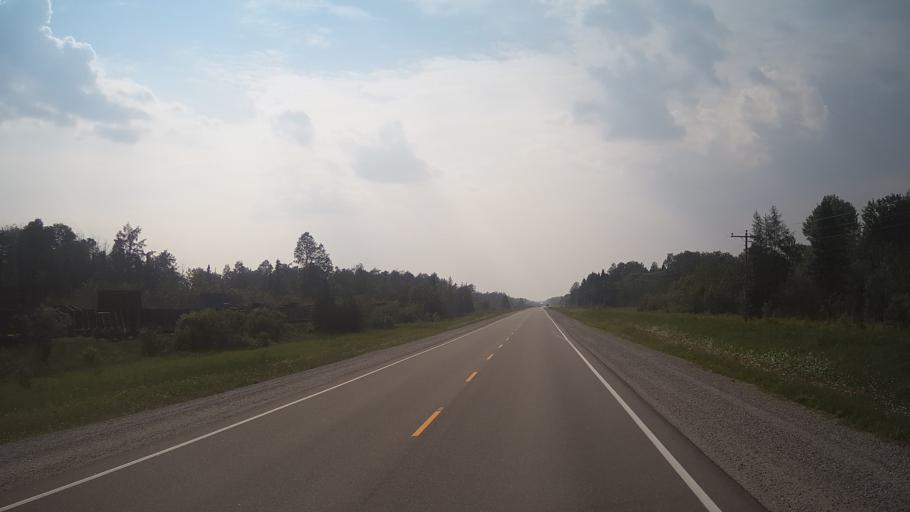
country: CA
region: Ontario
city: Kapuskasing
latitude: 49.5638
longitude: -83.0458
